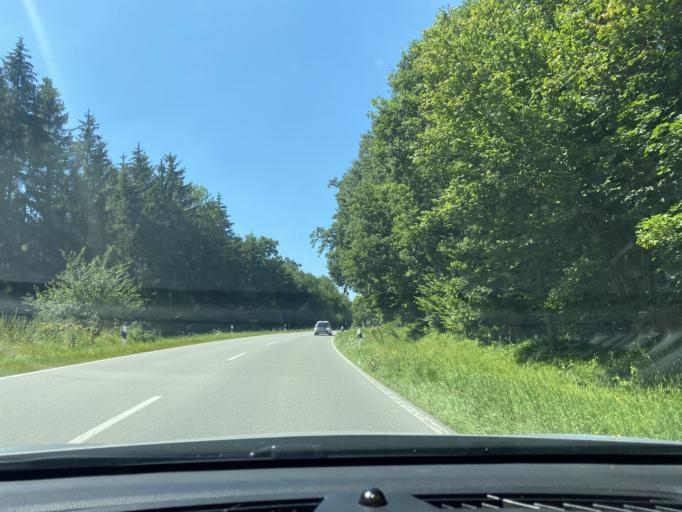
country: DE
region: Bavaria
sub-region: Upper Bavaria
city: Worth
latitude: 48.2641
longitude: 11.8803
